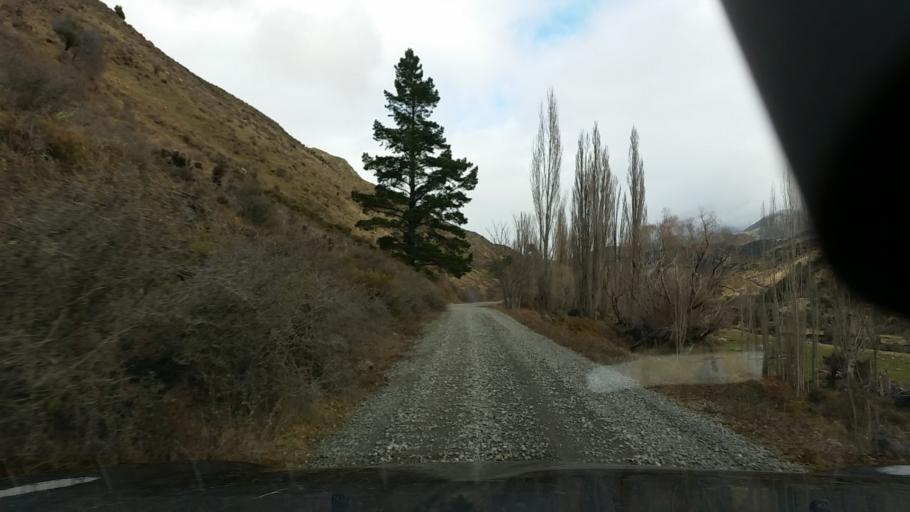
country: NZ
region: Tasman
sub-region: Tasman District
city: Brightwater
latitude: -41.7425
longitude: 173.4149
